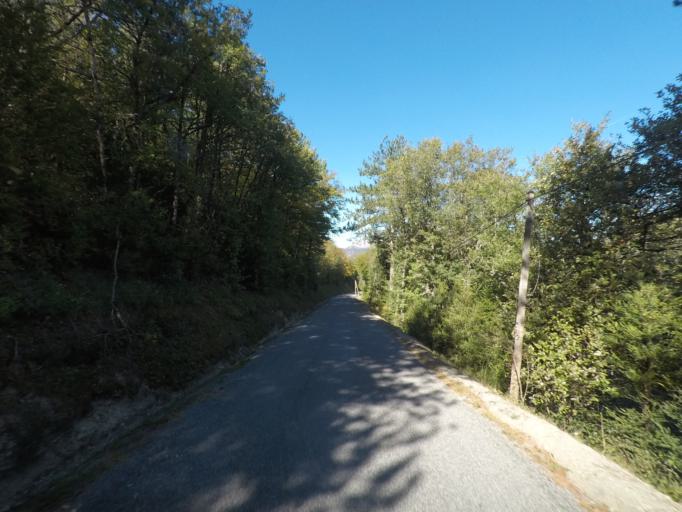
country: FR
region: Rhone-Alpes
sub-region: Departement de la Drome
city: Die
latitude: 44.5776
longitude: 5.2907
